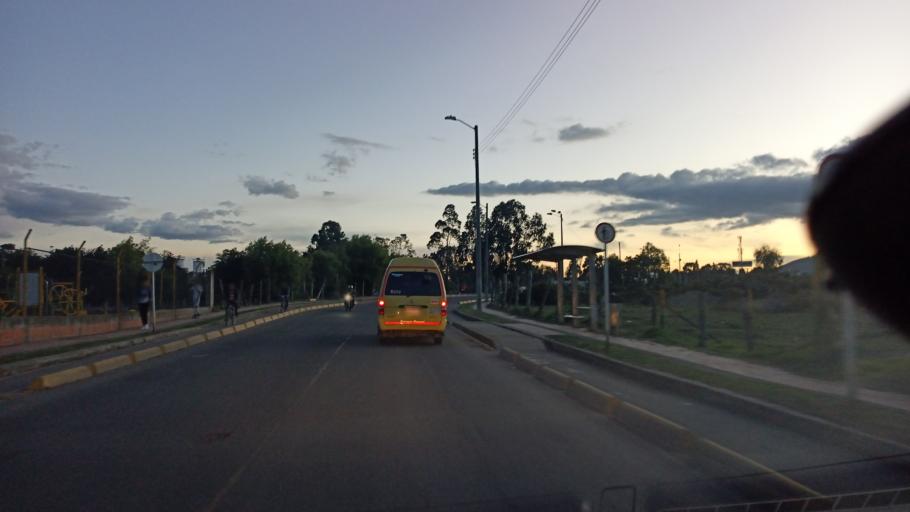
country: CO
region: Cundinamarca
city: Chia
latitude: 4.8569
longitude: -74.0670
